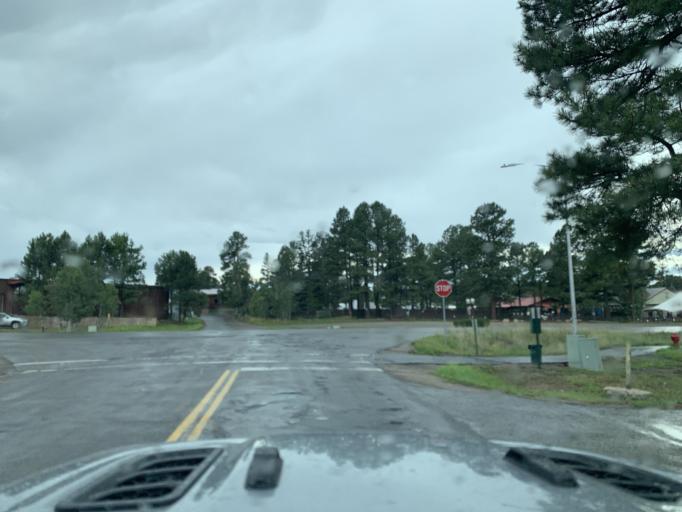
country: US
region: Colorado
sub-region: Archuleta County
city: Pagosa Springs
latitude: 37.2556
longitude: -107.0789
